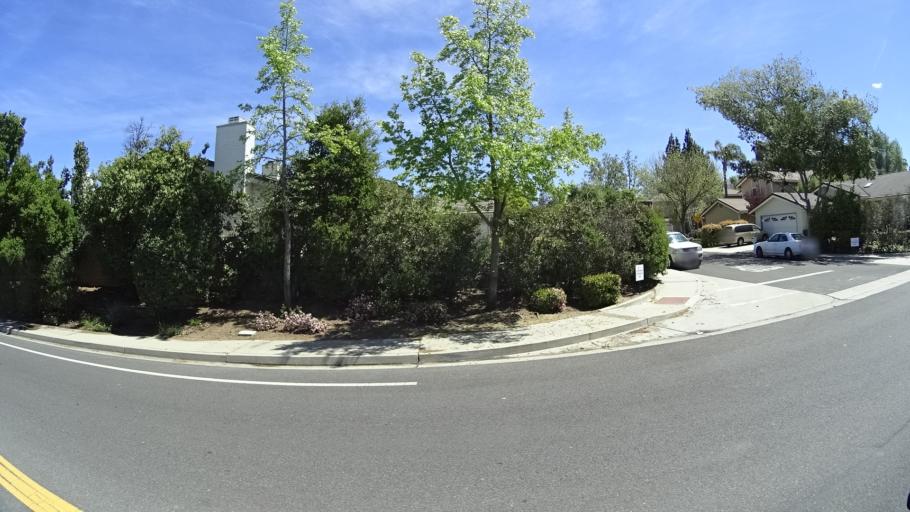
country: US
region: California
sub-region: Ventura County
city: Thousand Oaks
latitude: 34.2210
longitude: -118.8757
